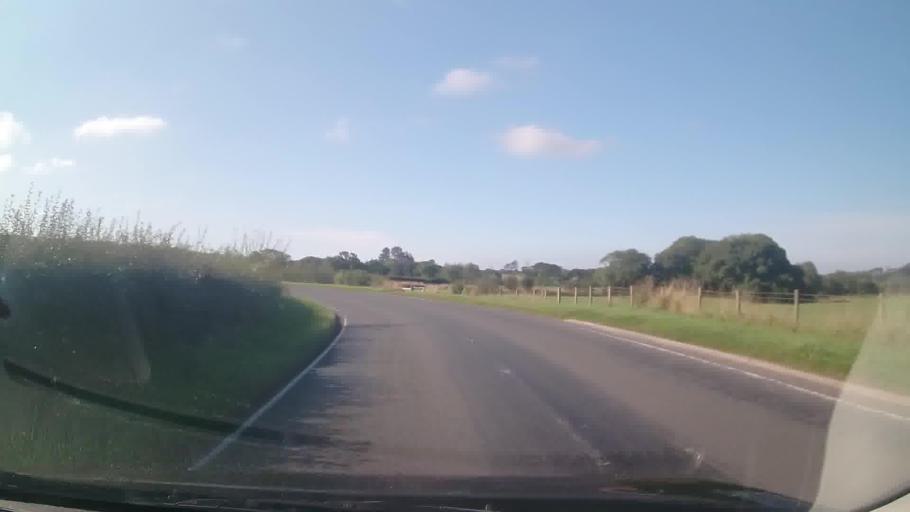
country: GB
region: England
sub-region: Cumbria
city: Seascale
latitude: 54.3458
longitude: -3.3658
